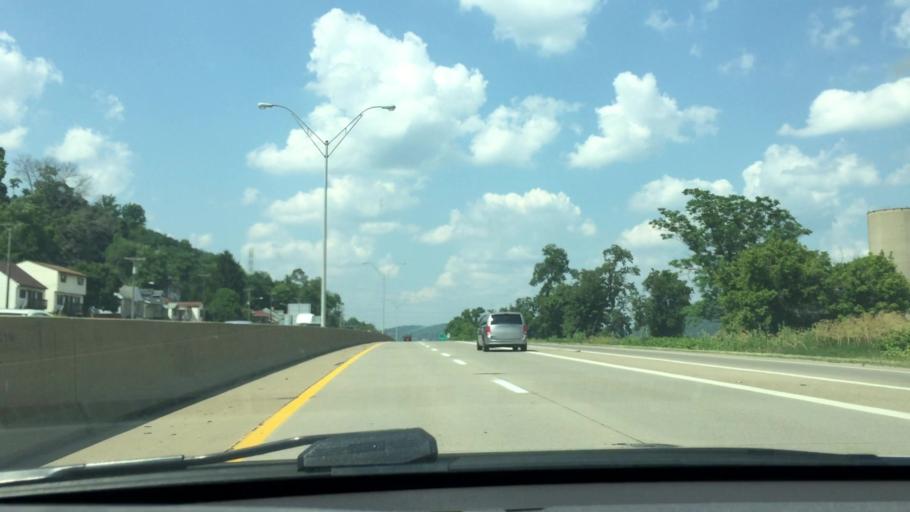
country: US
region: West Virginia
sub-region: Marshall County
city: Benwood
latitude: 40.0330
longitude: -80.7371
